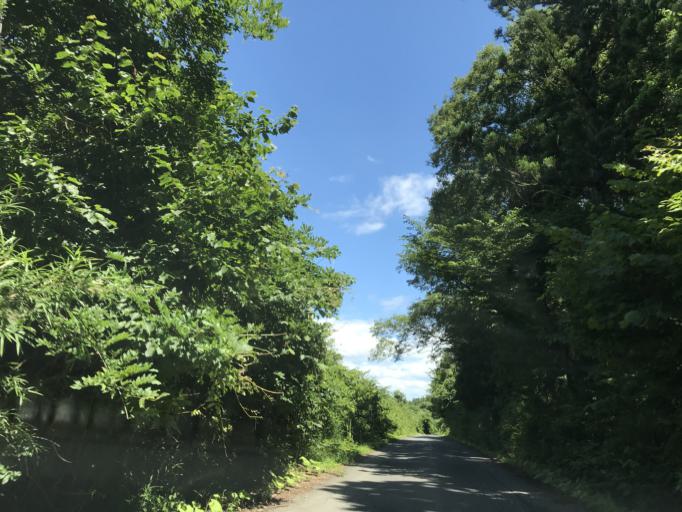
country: JP
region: Iwate
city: Ichinoseki
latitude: 38.9277
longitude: 141.0454
